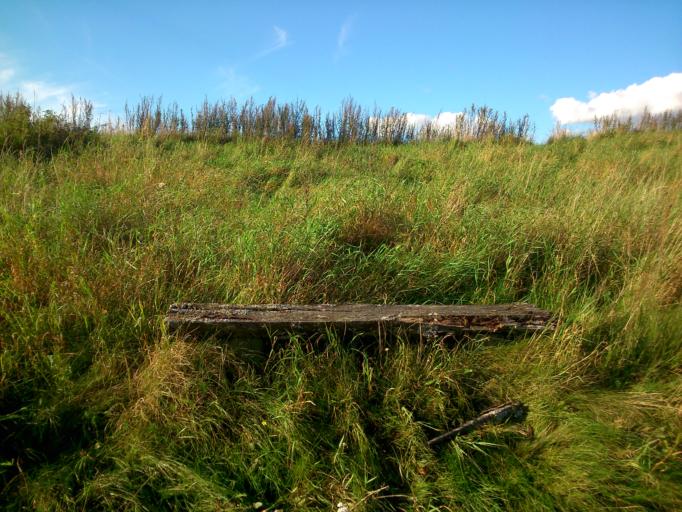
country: DK
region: Central Jutland
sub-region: Ringkobing-Skjern Kommune
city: Tarm
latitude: 55.9454
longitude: 8.5950
